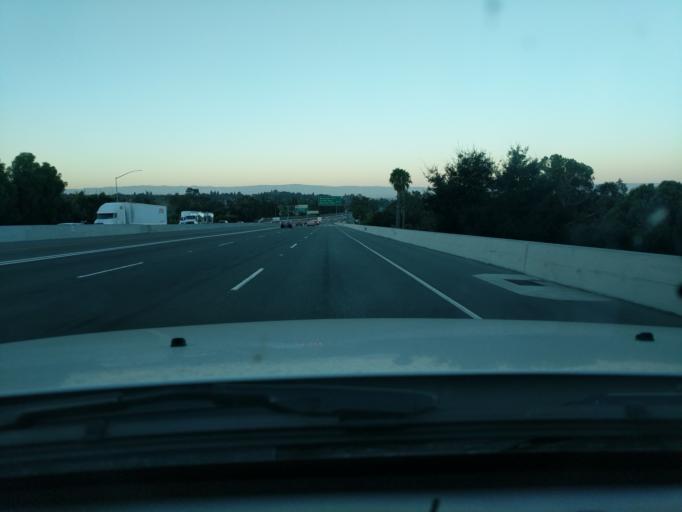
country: US
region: California
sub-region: Alameda County
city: Fremont
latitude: 37.5421
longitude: -121.9233
